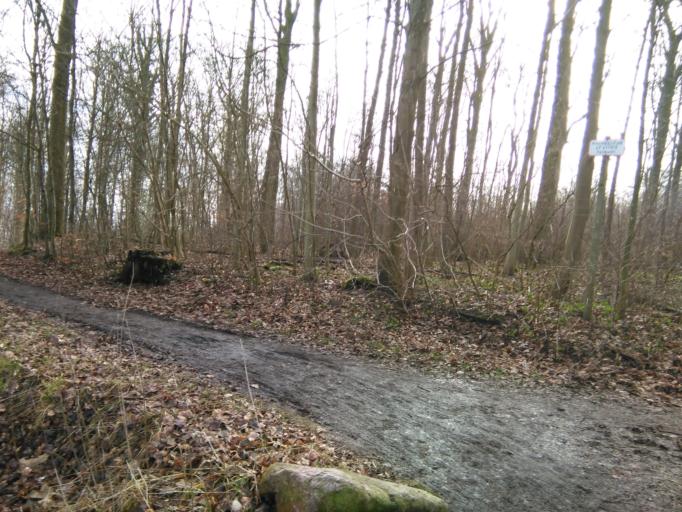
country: DK
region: Central Jutland
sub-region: Arhus Kommune
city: Arhus
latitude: 56.1817
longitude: 10.2318
